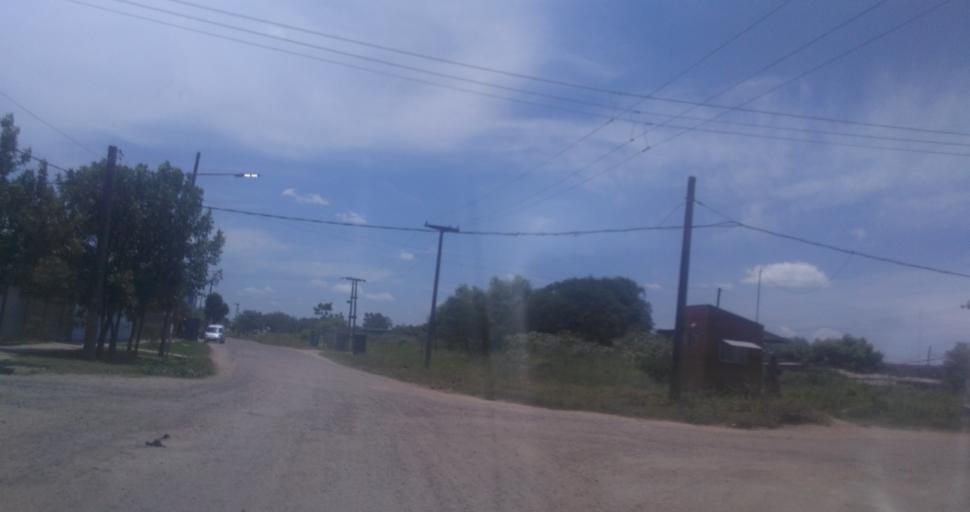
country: AR
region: Chaco
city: Fontana
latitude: -27.4189
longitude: -59.0381
